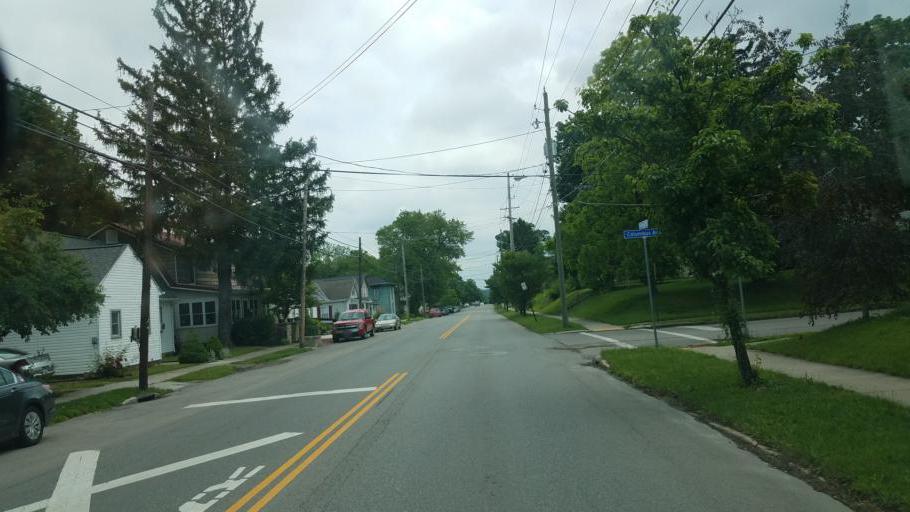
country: US
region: Ohio
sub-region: Delaware County
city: Delaware
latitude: 40.2994
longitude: -83.0812
